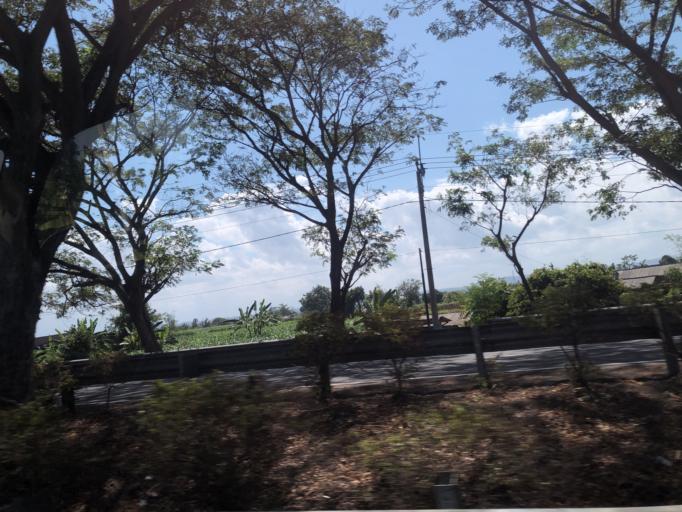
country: ID
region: Bali
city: Semarapura
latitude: -8.5675
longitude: 115.4117
